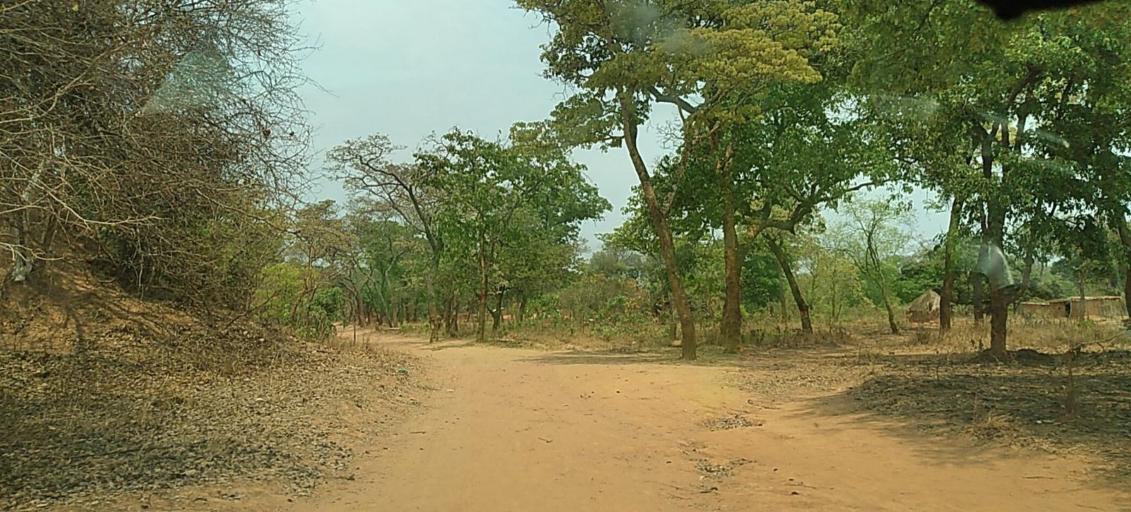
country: ZM
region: North-Western
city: Kabompo
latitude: -13.5731
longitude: 24.4396
